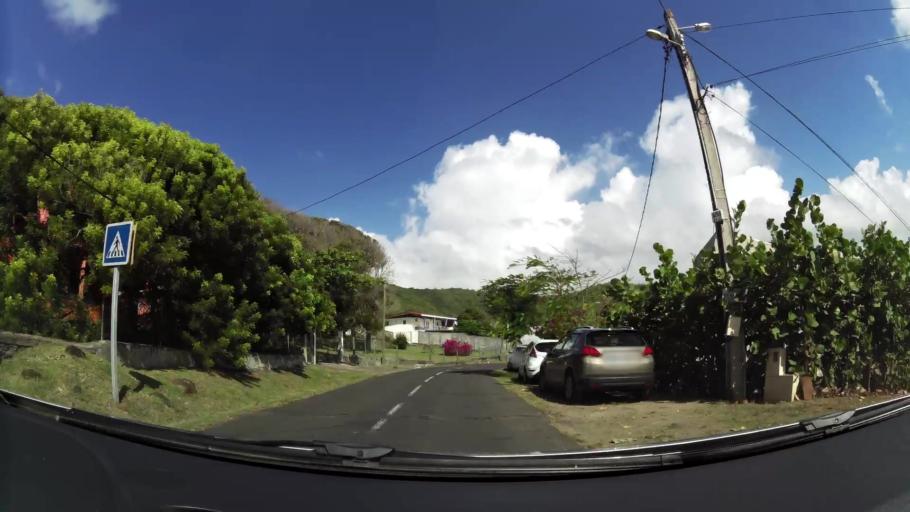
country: MQ
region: Martinique
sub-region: Martinique
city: Les Trois-Ilets
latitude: 14.4687
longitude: -61.0467
